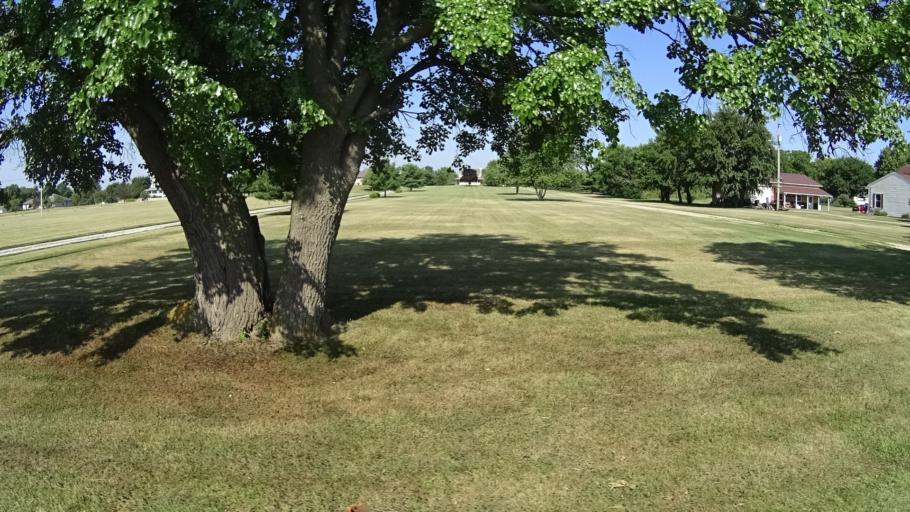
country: US
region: Ohio
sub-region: Huron County
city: Bellevue
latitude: 41.3666
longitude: -82.8189
